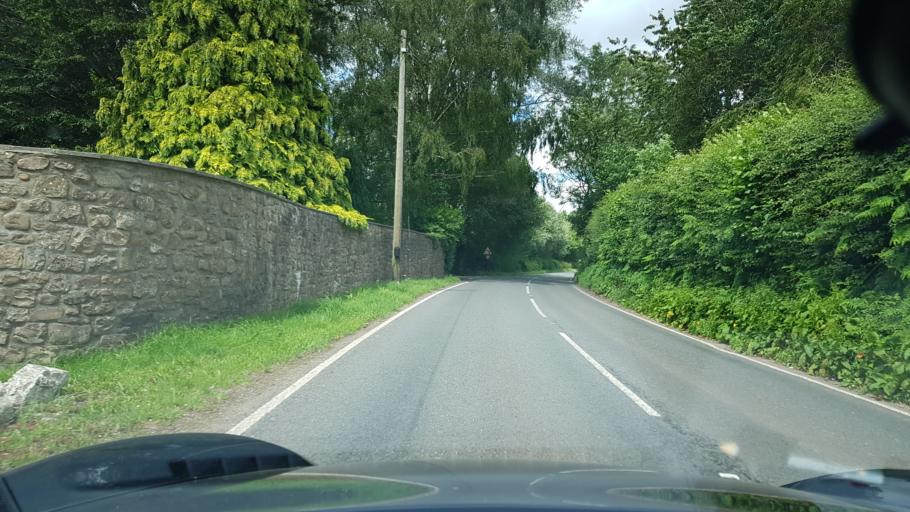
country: GB
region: Wales
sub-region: Monmouthshire
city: Llanarth
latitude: 51.7488
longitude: -2.9457
